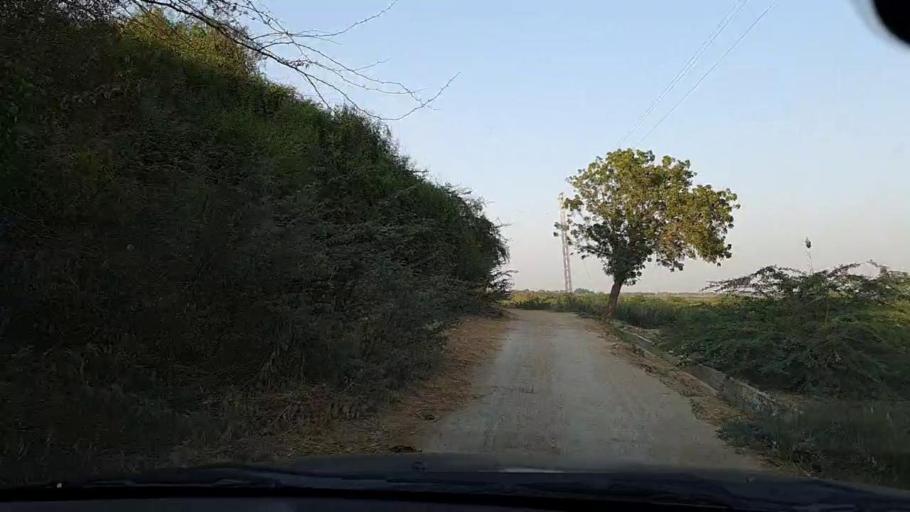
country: PK
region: Sindh
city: Thatta
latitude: 24.5617
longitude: 67.8801
